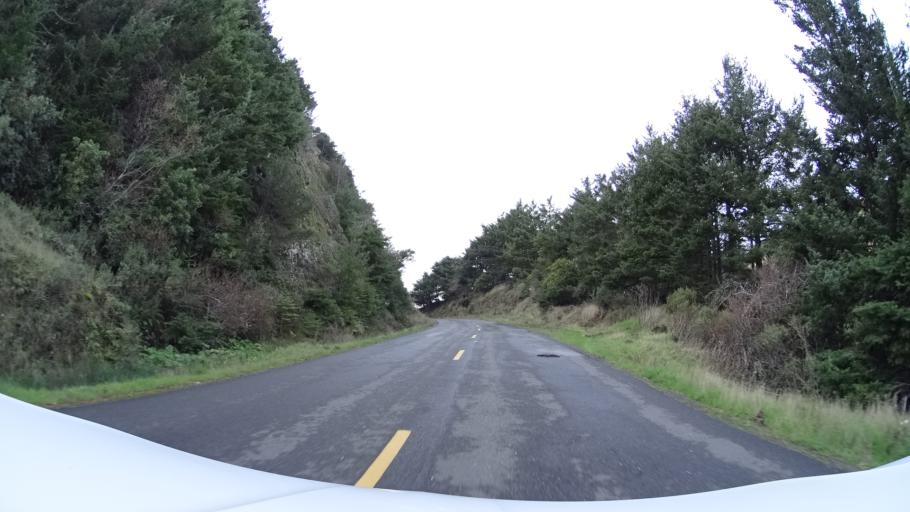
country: US
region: California
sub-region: Humboldt County
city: Ferndale
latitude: 40.3478
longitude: -124.3546
